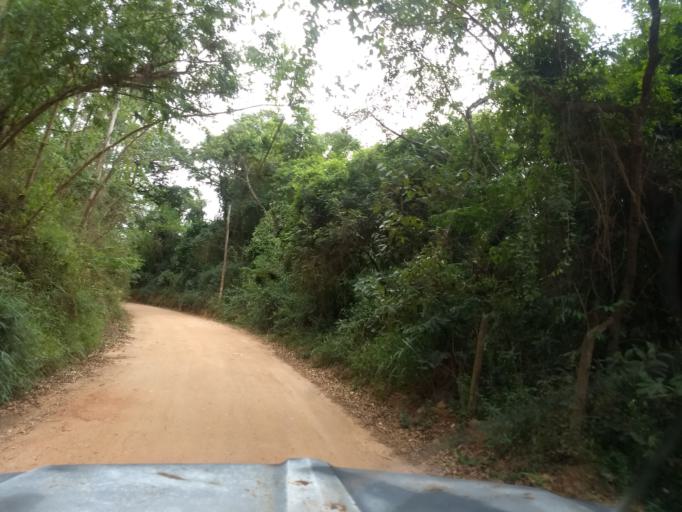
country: BR
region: Sao Paulo
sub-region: Cabreuva
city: Cabreuva
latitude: -23.4072
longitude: -47.1969
